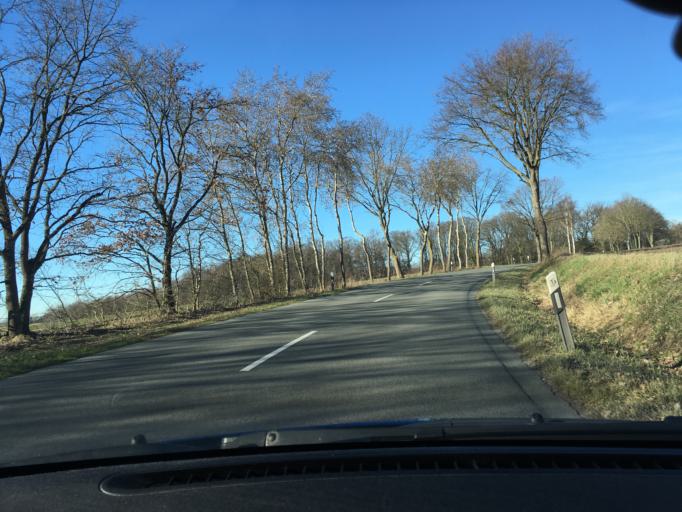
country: DE
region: Lower Saxony
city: Schwienau
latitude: 52.9745
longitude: 10.4484
